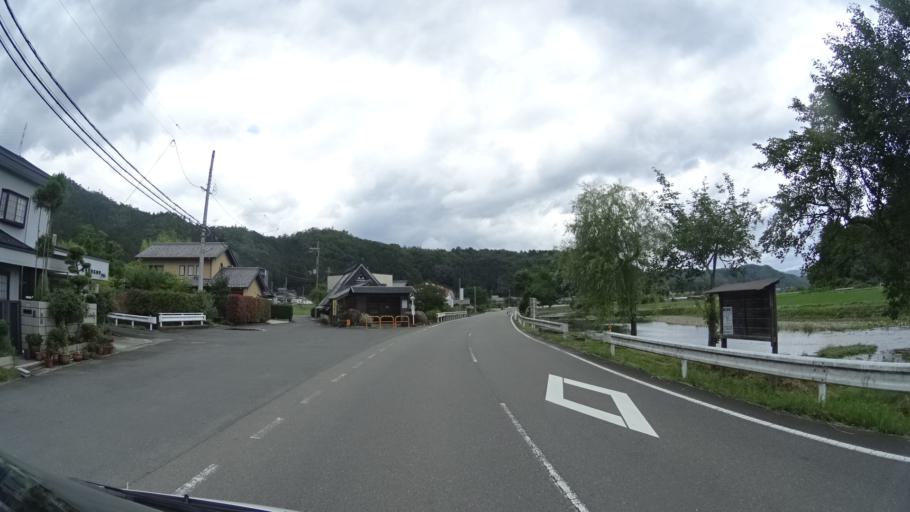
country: JP
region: Kyoto
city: Kameoka
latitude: 35.1026
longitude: 135.4351
